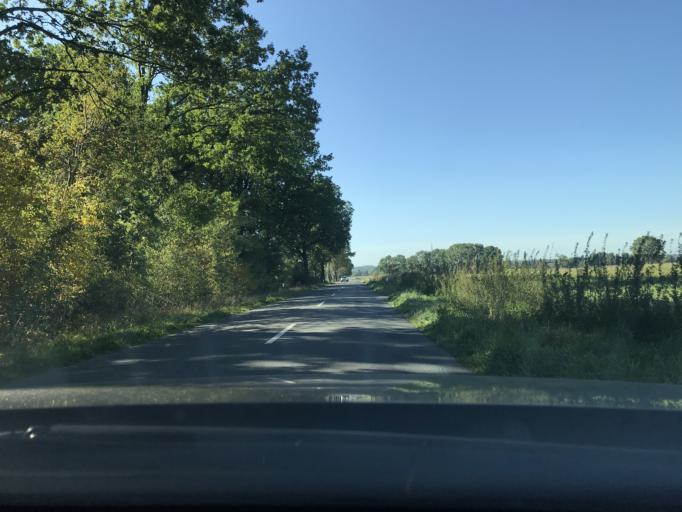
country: DE
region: Lower Saxony
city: Gerdau
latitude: 52.9771
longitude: 10.4329
